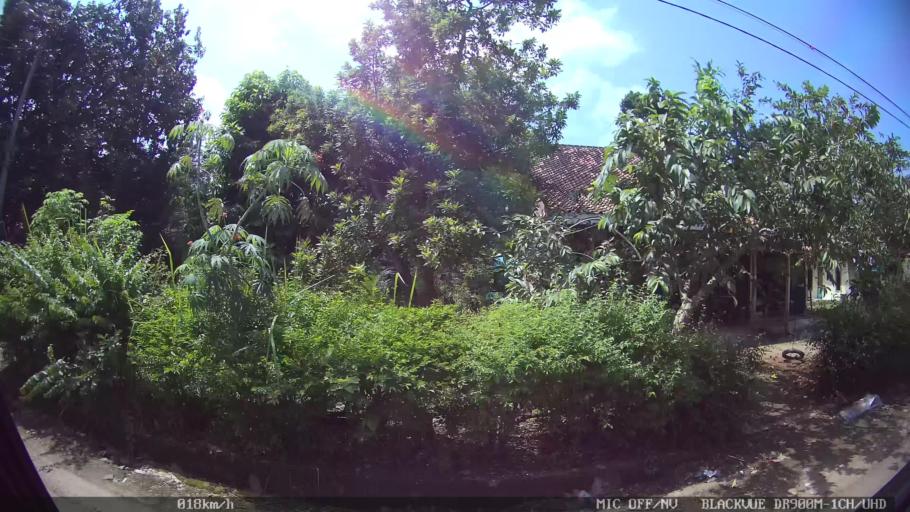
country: ID
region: Lampung
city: Kedaton
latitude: -5.3544
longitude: 105.2861
